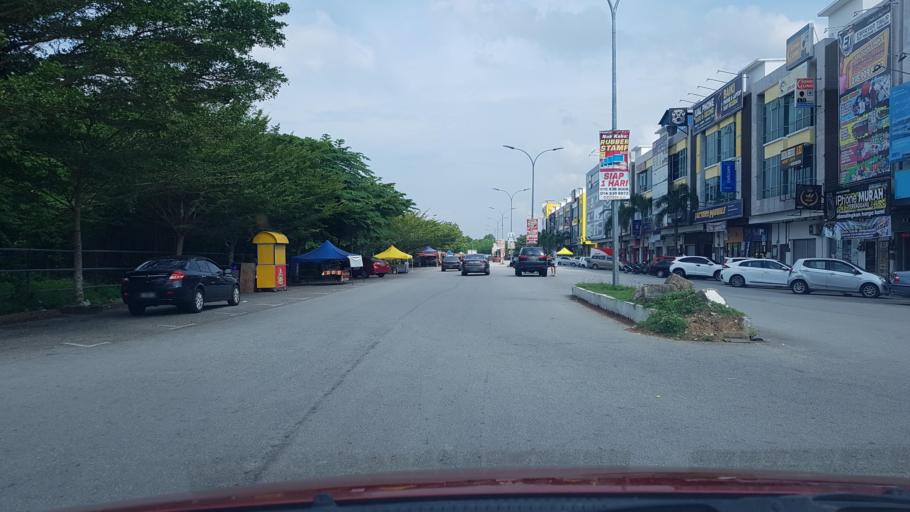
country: MY
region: Terengganu
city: Kuala Terengganu
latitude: 5.3584
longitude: 103.0964
